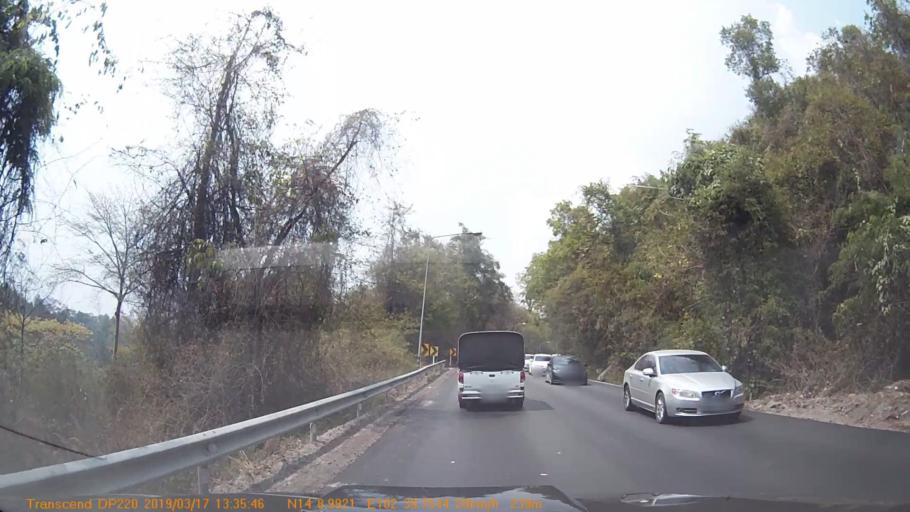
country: TH
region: Buriram
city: Non Din Daeng
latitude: 14.1500
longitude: 102.6625
